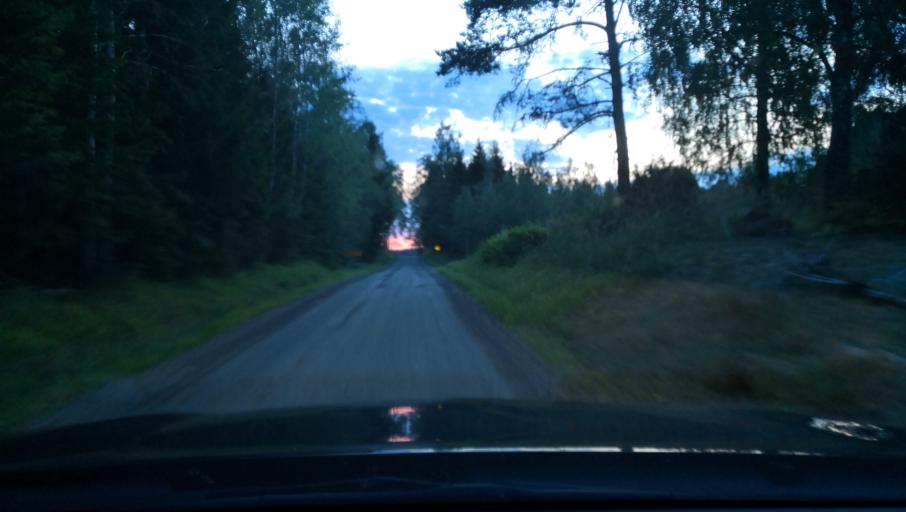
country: SE
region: Uppsala
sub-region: Osthammars Kommun
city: Bjorklinge
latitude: 60.0051
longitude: 17.3377
